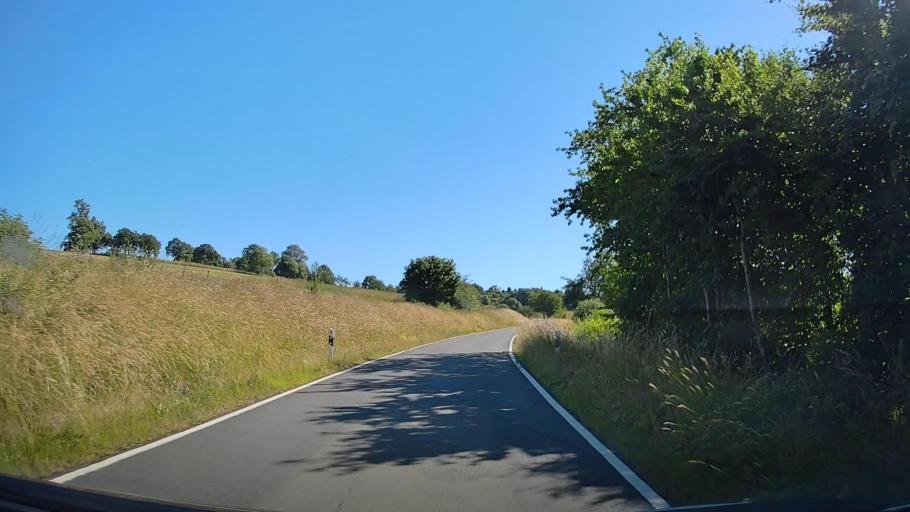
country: DE
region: Lower Saxony
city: Vahlbruch
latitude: 51.9749
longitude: 9.3535
